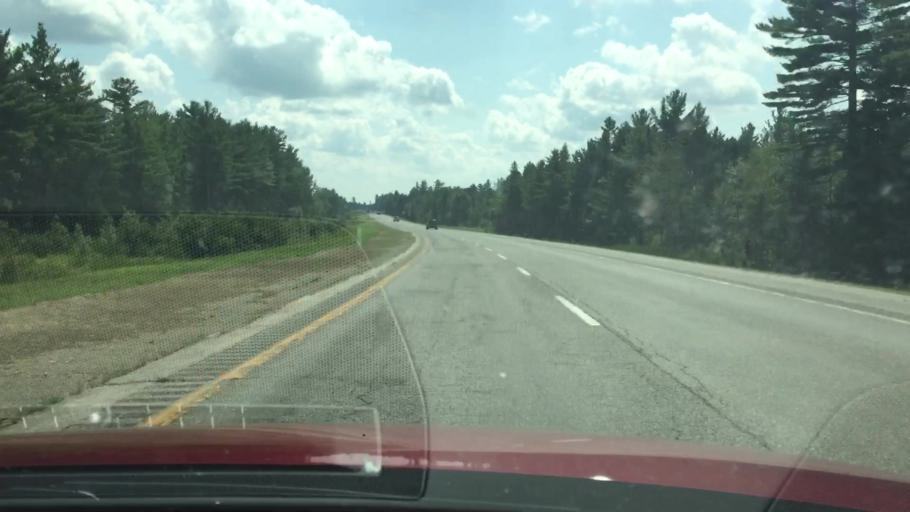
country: US
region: Maine
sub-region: Penobscot County
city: Medway
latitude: 45.5893
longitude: -68.5426
